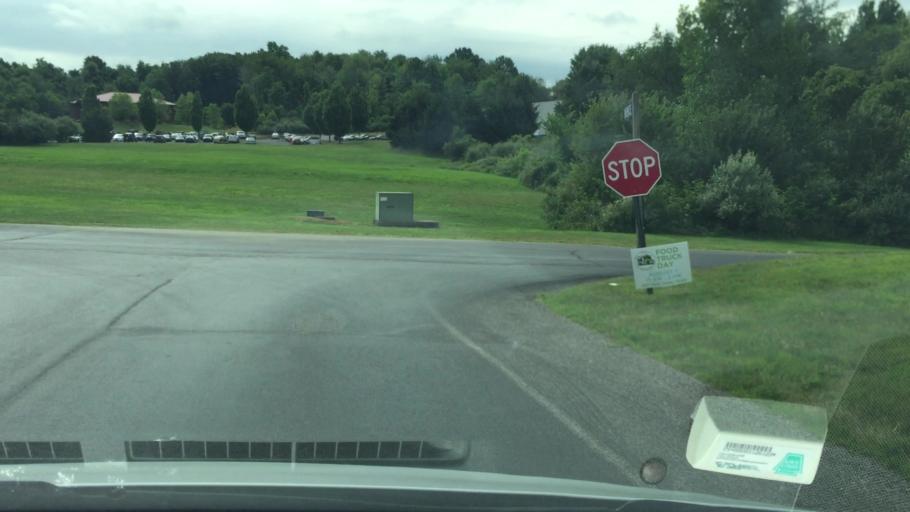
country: US
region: Pennsylvania
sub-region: Armstrong County
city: Apollo
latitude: 40.5312
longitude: -79.6482
